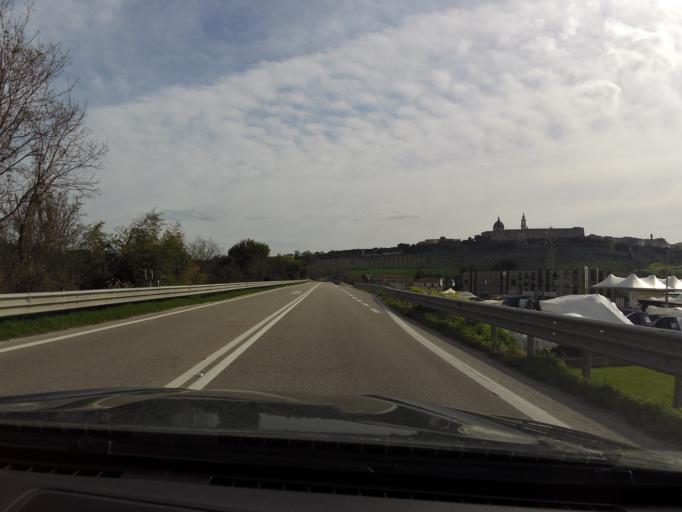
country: IT
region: The Marches
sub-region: Provincia di Ancona
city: Villa Musone
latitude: 43.4513
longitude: 13.6107
